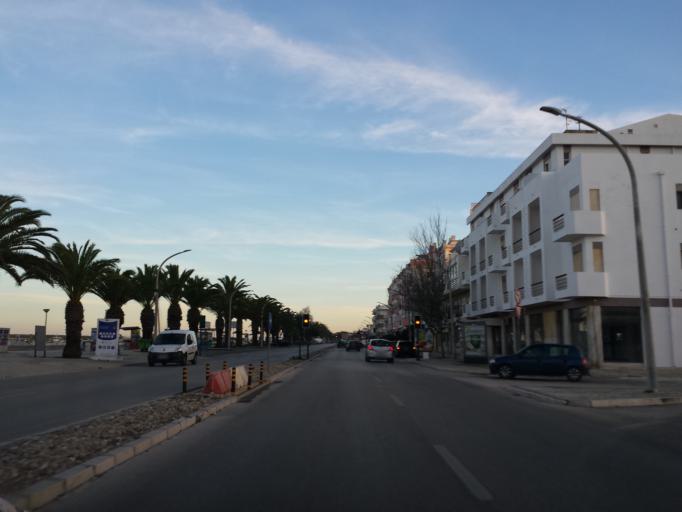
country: PT
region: Faro
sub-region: Lagos
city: Lagos
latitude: 37.1077
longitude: -8.6753
